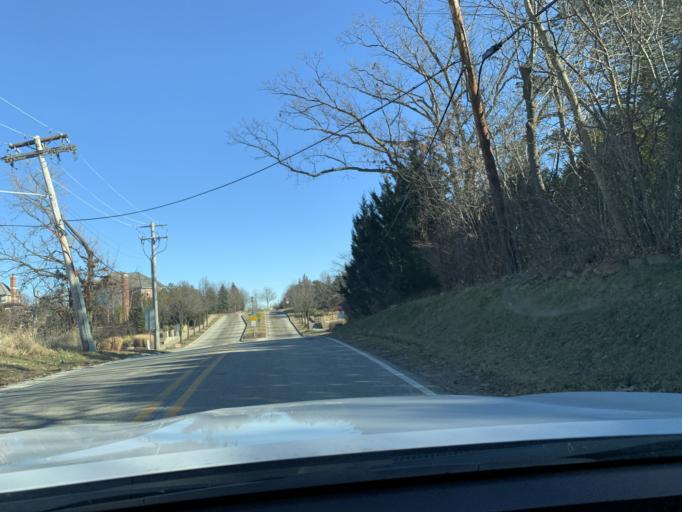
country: US
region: Illinois
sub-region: DuPage County
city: Burr Ridge
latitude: 41.7311
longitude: -87.9156
